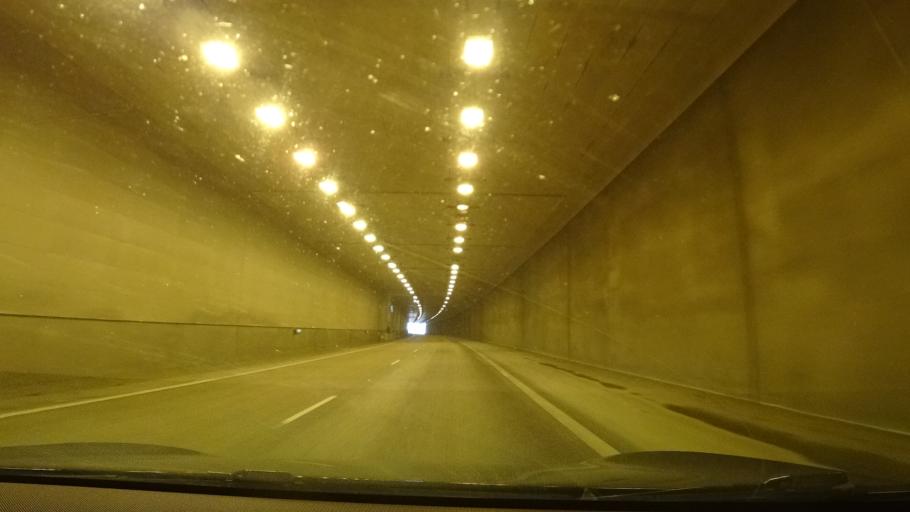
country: FI
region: Kymenlaakso
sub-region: Kotka-Hamina
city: Hamina
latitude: 60.5968
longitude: 27.1758
